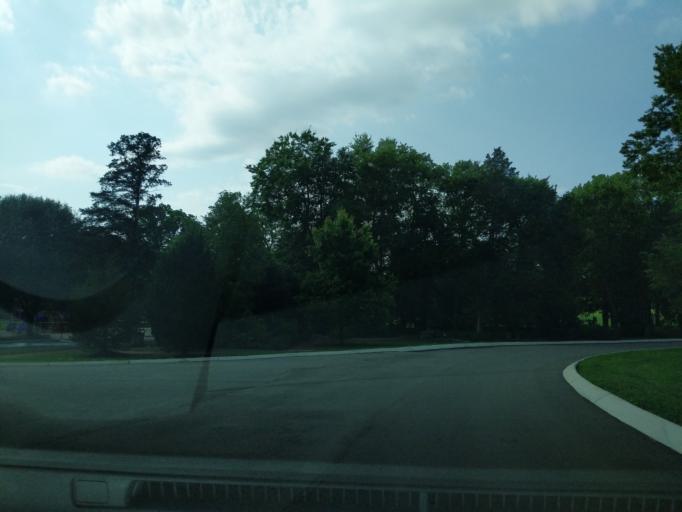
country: US
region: Tennessee
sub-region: Cheatham County
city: Pegram
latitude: 36.0290
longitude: -86.9577
